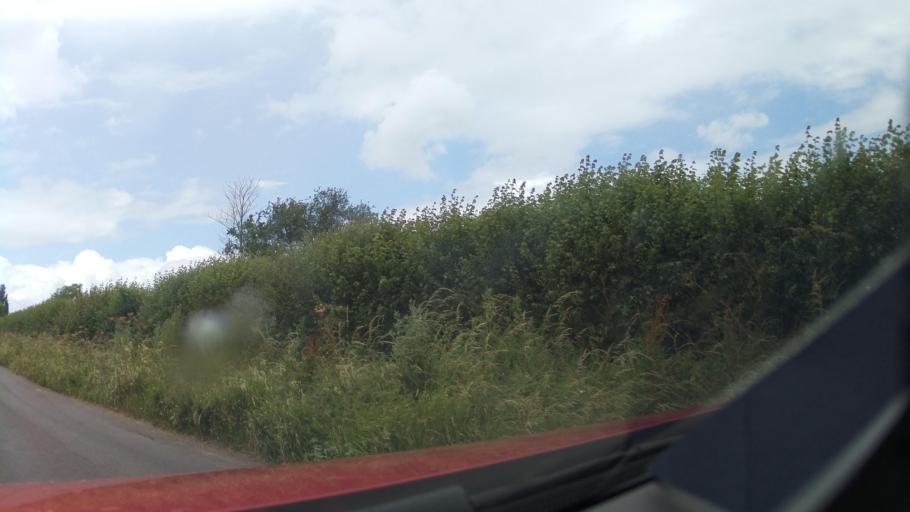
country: GB
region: England
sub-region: Wiltshire
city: Malmesbury
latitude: 51.5390
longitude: -2.0753
